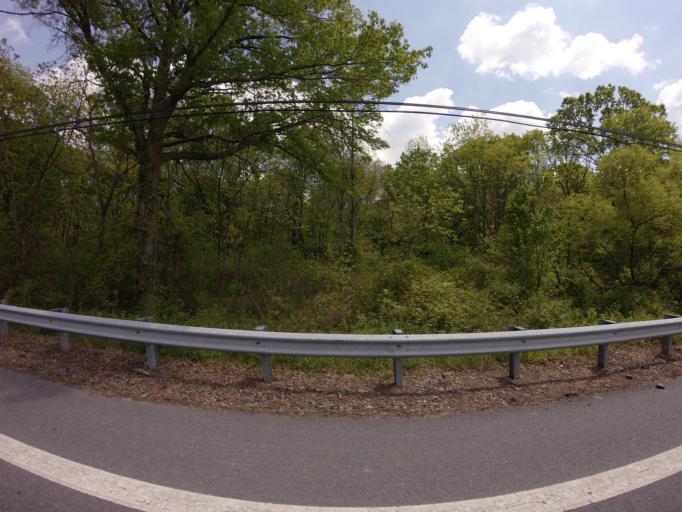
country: US
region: Maryland
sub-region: Frederick County
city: Green Valley
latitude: 39.3189
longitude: -77.2882
